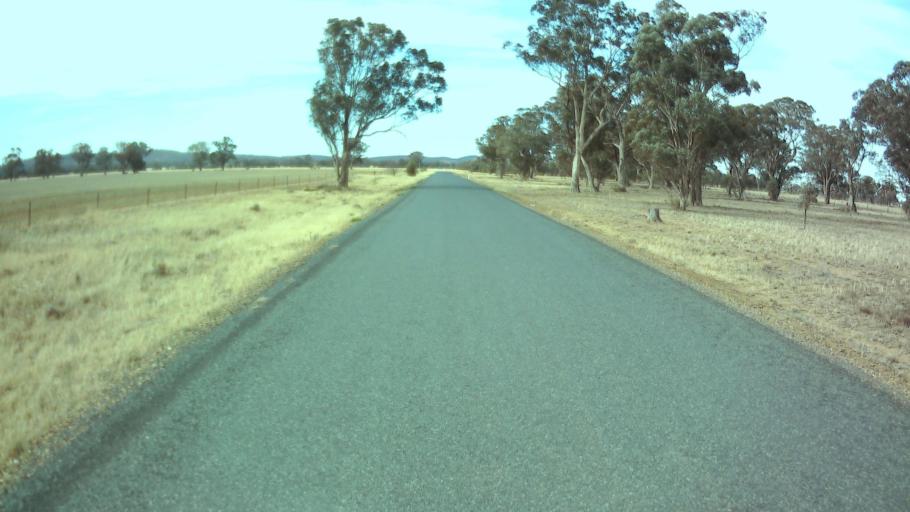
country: AU
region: New South Wales
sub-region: Weddin
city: Grenfell
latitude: -33.8596
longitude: 147.8601
